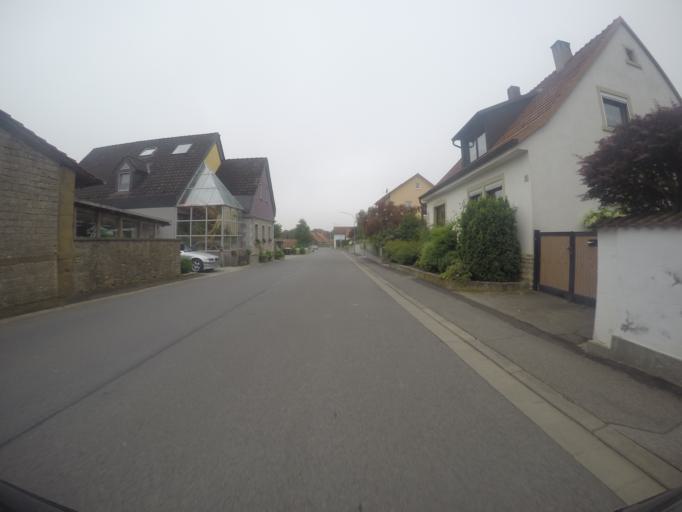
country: DE
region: Bavaria
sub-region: Regierungsbezirk Unterfranken
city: Schwanfeld
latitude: 49.9222
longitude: 10.1421
